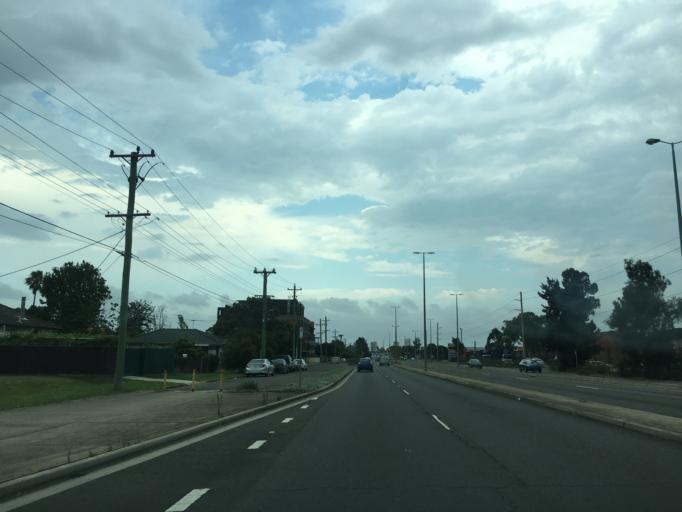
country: AU
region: New South Wales
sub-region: Liverpool
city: Miller
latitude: -33.9275
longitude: 150.8848
